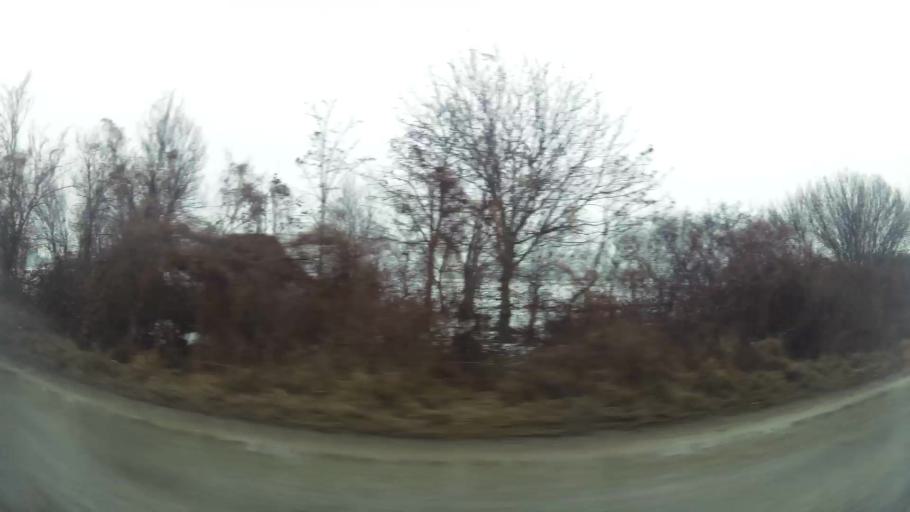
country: MK
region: Ilinden
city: Idrizovo
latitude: 41.9518
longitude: 21.5831
